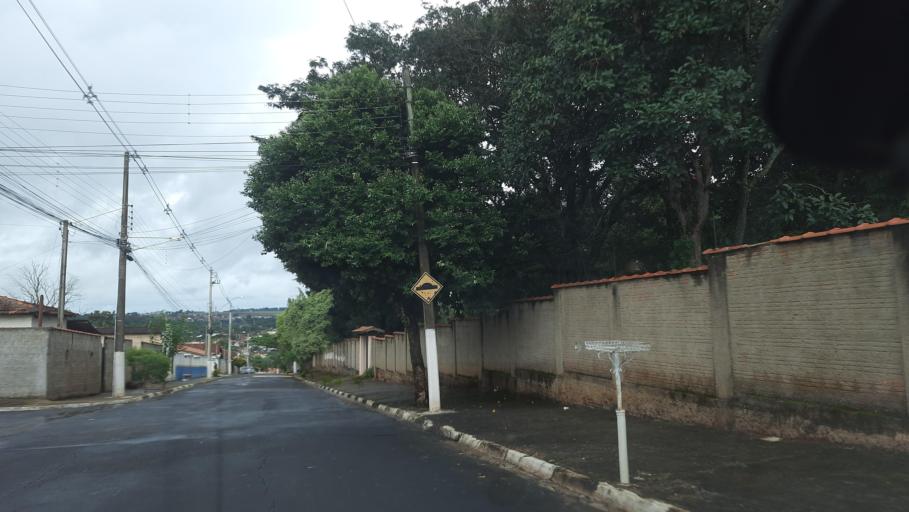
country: BR
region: Sao Paulo
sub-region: Casa Branca
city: Casa Branca
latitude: -21.7737
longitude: -47.0965
